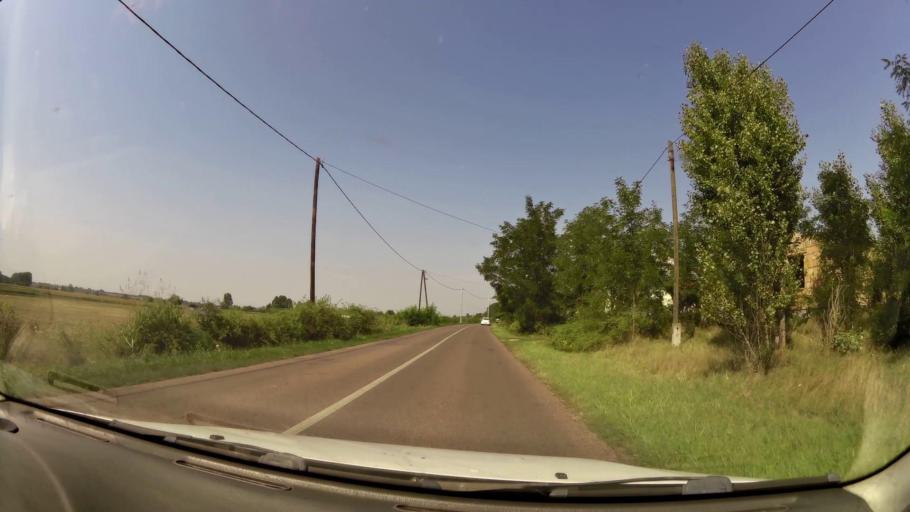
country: HU
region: Pest
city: Tapiobicske
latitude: 47.3727
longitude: 19.6745
